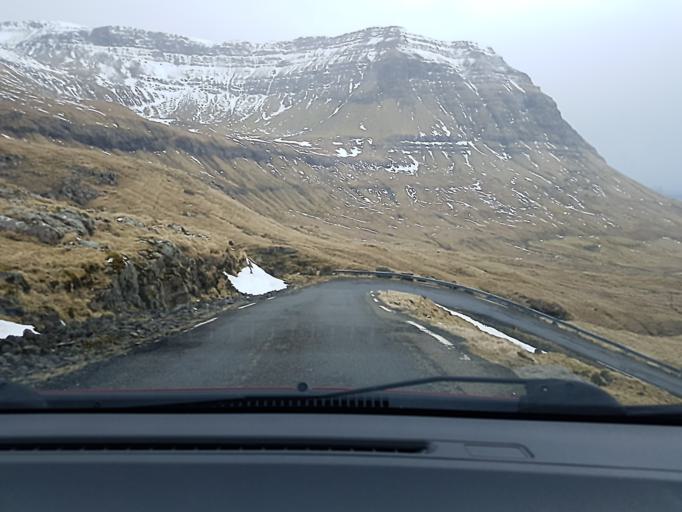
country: FO
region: Streymoy
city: Kollafjordhur
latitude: 62.0471
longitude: -6.9222
